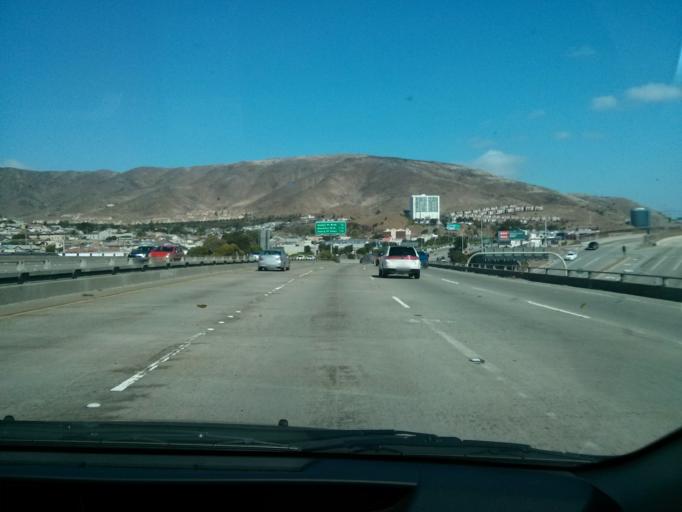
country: US
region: California
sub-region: San Mateo County
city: South San Francisco
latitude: 37.6540
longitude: -122.4069
